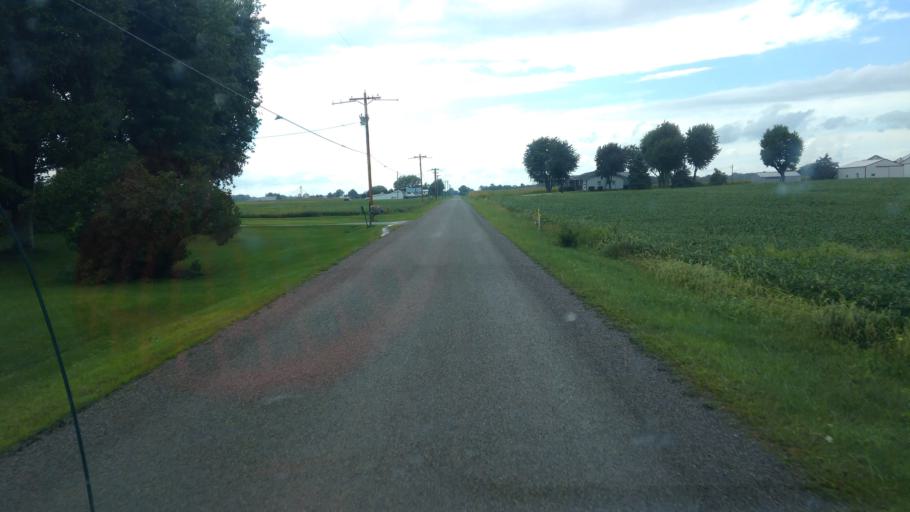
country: US
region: Ohio
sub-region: Hardin County
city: Kenton
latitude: 40.7040
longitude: -83.6356
